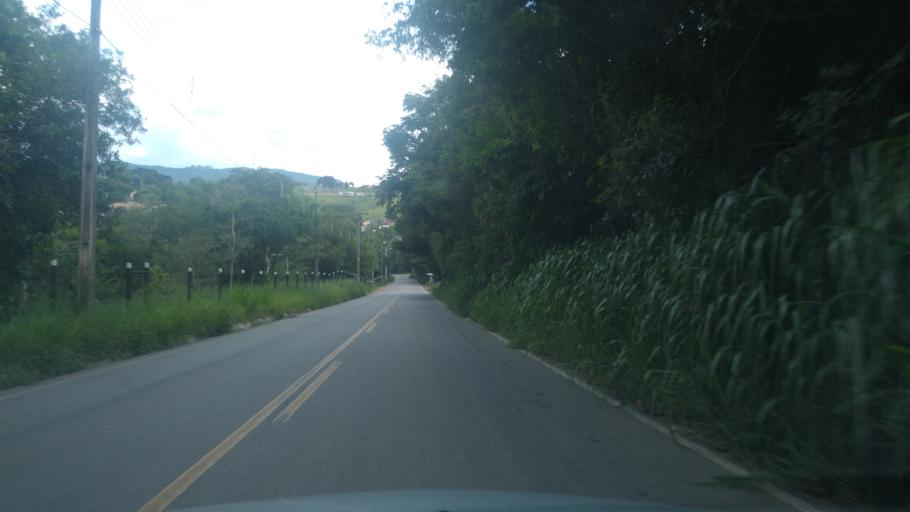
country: BR
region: Minas Gerais
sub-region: Extrema
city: Extrema
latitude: -22.8085
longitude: -46.3127
